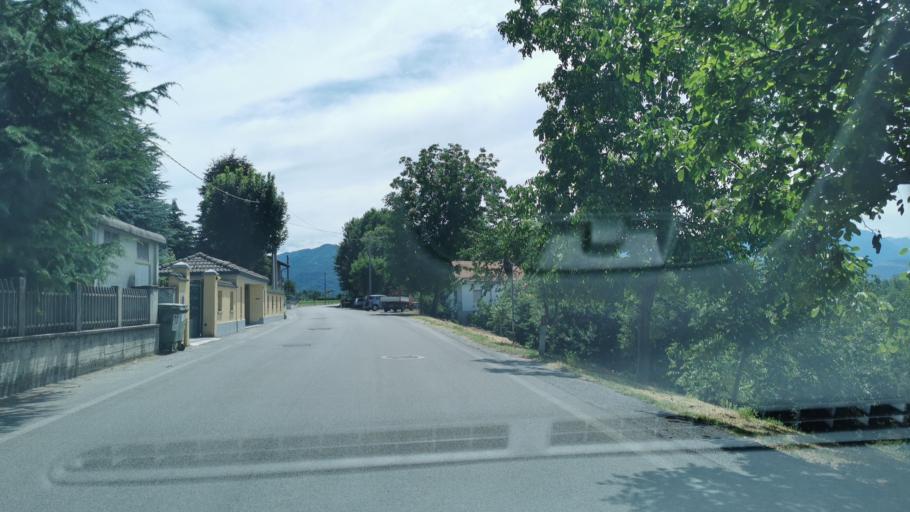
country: IT
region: Piedmont
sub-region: Provincia di Cuneo
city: Cuneo
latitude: 44.3763
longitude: 7.5675
